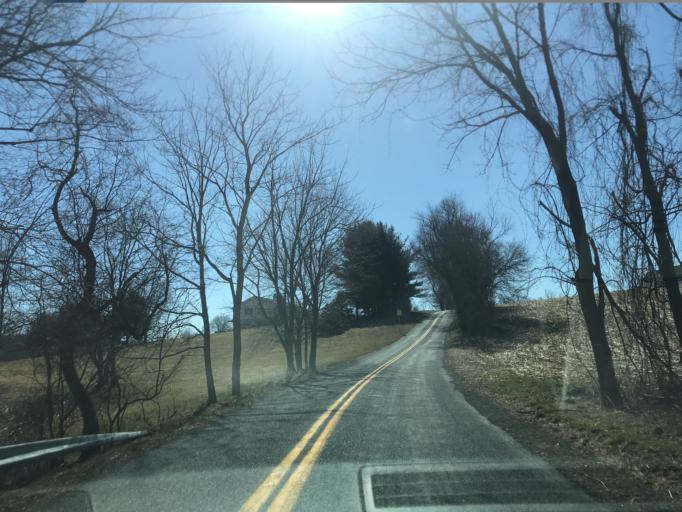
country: US
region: Pennsylvania
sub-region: York County
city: Stewartstown
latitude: 39.7098
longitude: -76.5223
